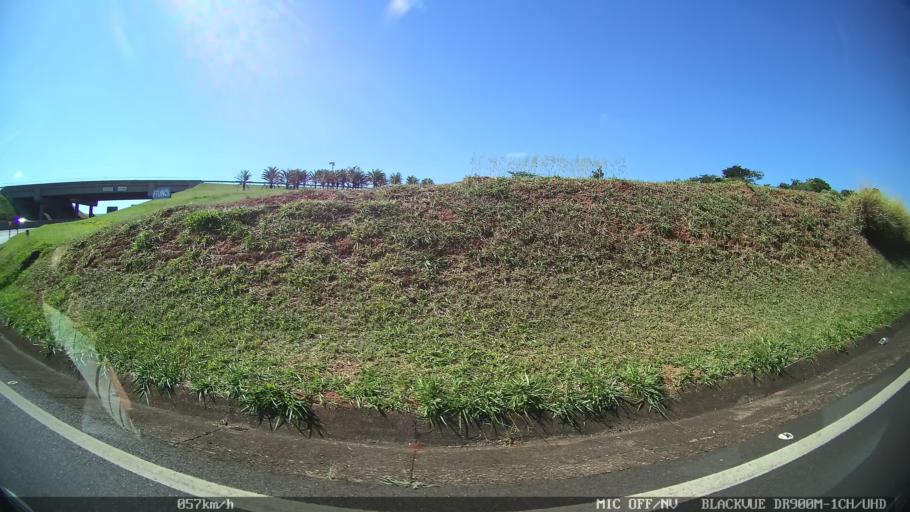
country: BR
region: Sao Paulo
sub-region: Franca
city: Franca
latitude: -20.5628
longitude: -47.4139
